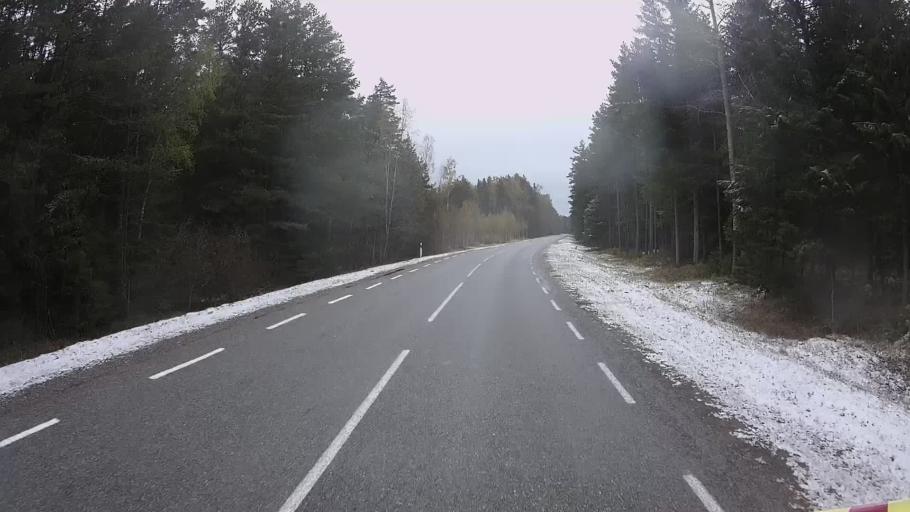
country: EE
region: Hiiumaa
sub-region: Kaerdla linn
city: Kardla
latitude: 59.0296
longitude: 22.6733
